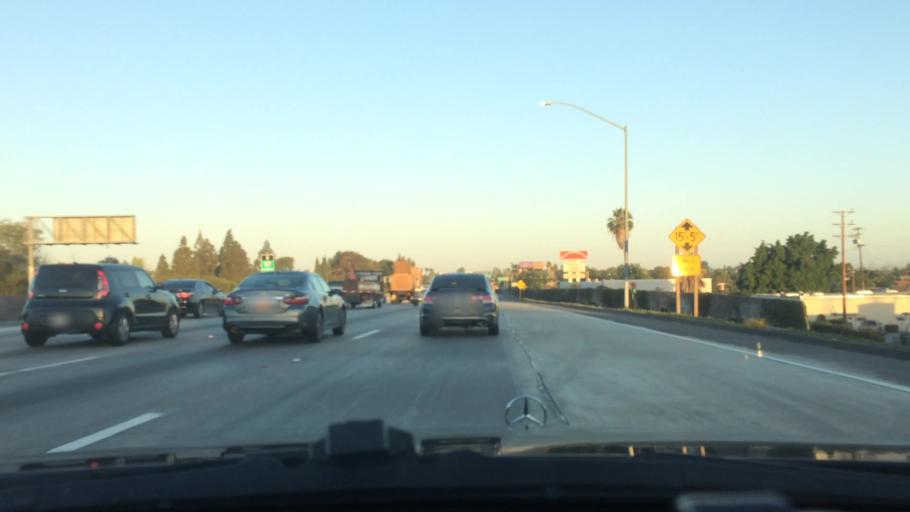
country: US
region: California
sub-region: Los Angeles County
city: Artesia
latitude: 33.8769
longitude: -118.0735
